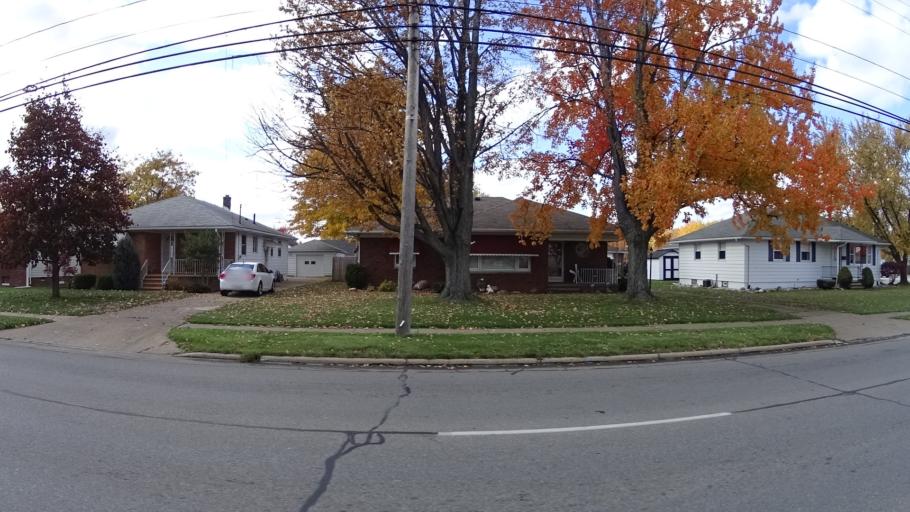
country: US
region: Ohio
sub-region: Lorain County
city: Lorain
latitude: 41.4392
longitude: -82.1854
